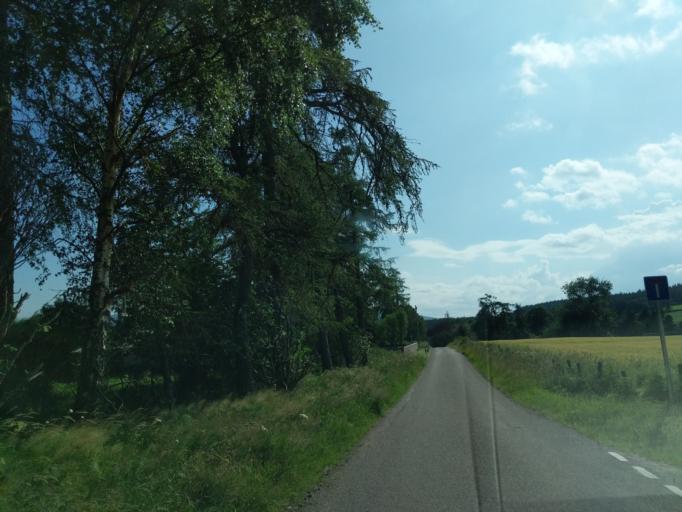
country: GB
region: Scotland
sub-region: Moray
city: Rothes
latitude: 57.4806
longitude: -3.2347
